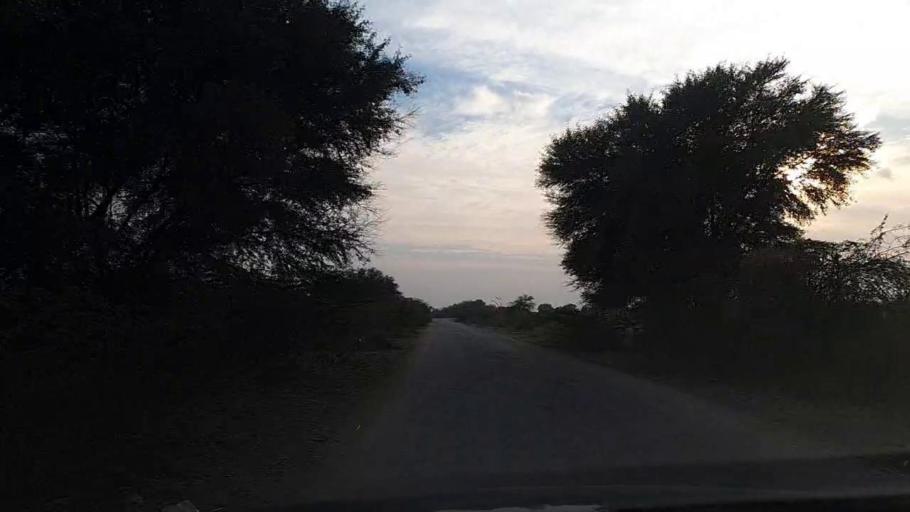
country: PK
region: Sindh
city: Nawabshah
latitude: 26.4009
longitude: 68.4812
